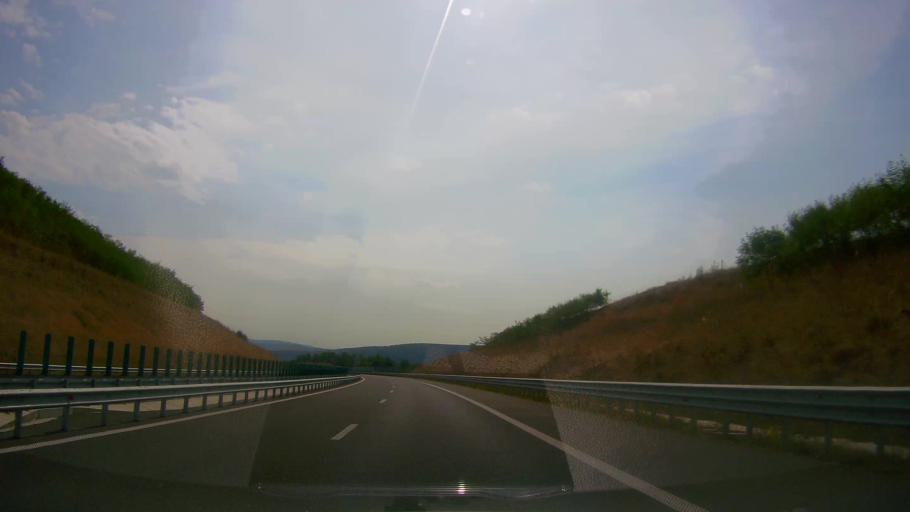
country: RO
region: Cluj
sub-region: Comuna Gilau
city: Gilau
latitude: 46.7667
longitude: 23.3846
